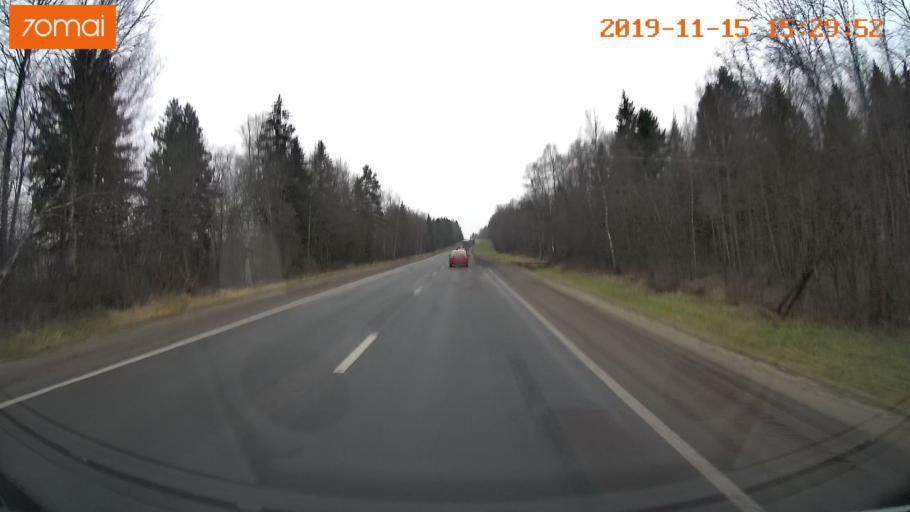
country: RU
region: Jaroslavl
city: Danilov
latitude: 58.1159
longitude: 40.1166
